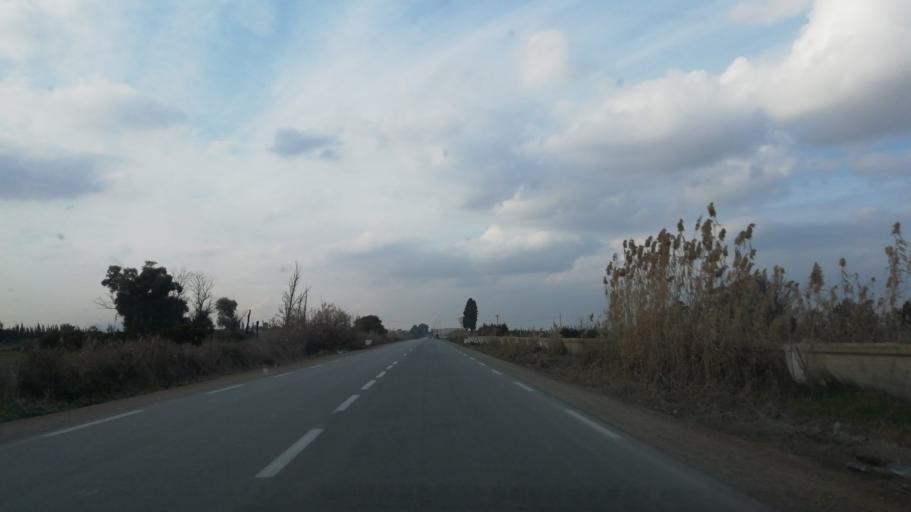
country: DZ
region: Mascara
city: Sig
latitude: 35.6504
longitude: 0.0225
